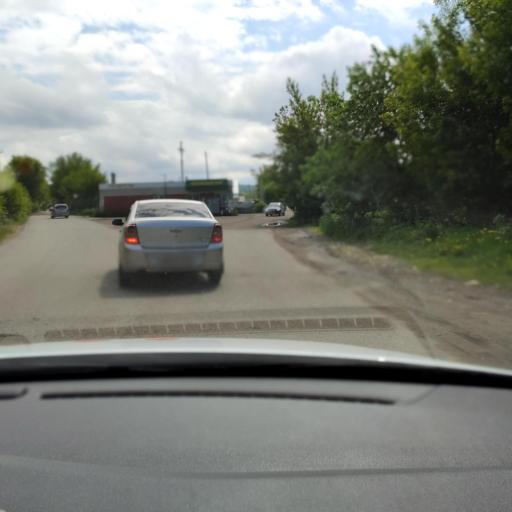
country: RU
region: Tatarstan
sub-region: Gorod Kazan'
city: Kazan
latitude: 55.7025
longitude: 49.0852
